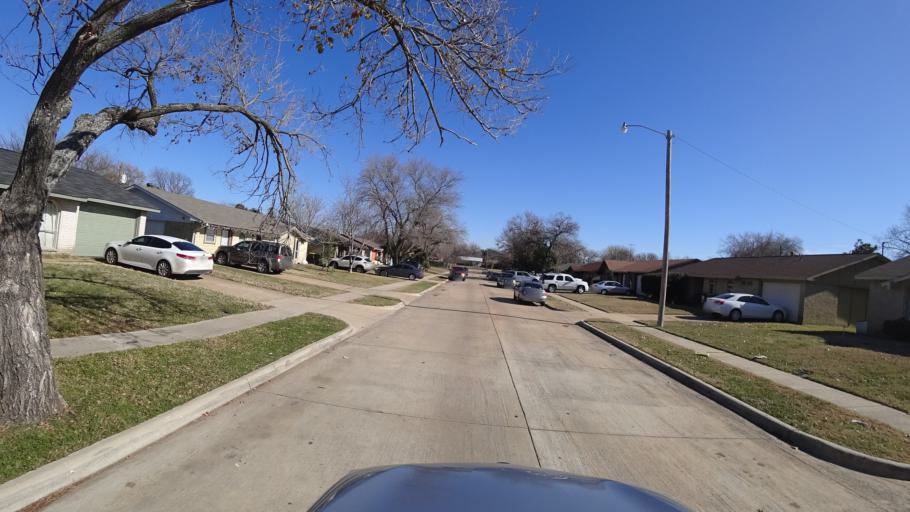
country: US
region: Texas
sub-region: Denton County
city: Lewisville
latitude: 33.0339
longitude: -97.0232
